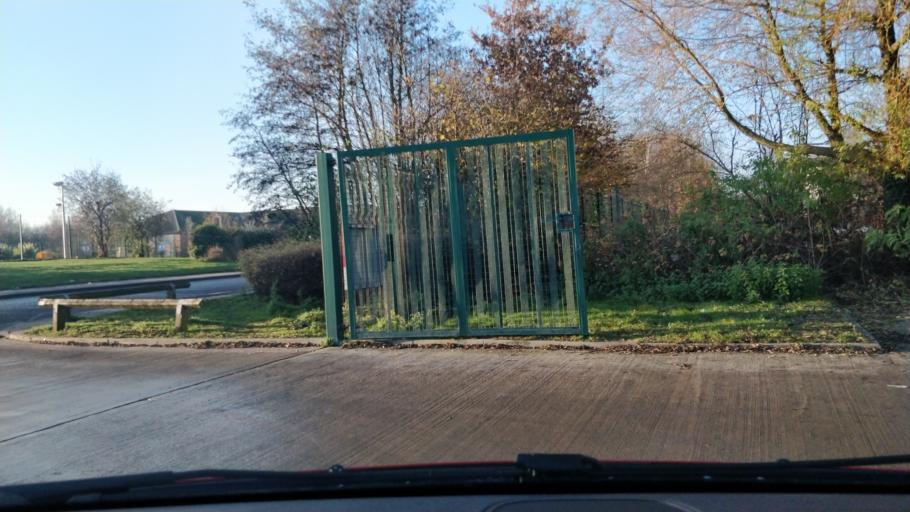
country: GB
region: England
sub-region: Sefton
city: Southport
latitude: 53.6272
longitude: -2.9868
